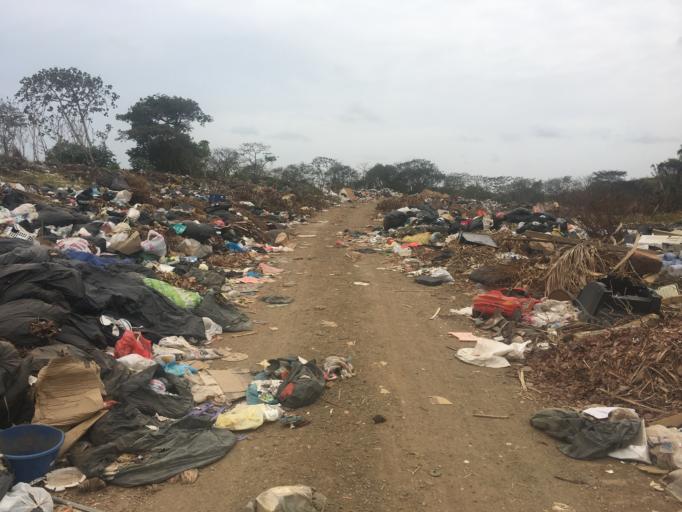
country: PA
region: Los Santos
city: Pedasi
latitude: 7.5479
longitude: -80.0811
